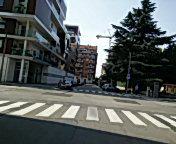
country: IT
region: Piedmont
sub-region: Provincia di Torino
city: Lesna
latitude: 45.0342
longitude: 7.6503
